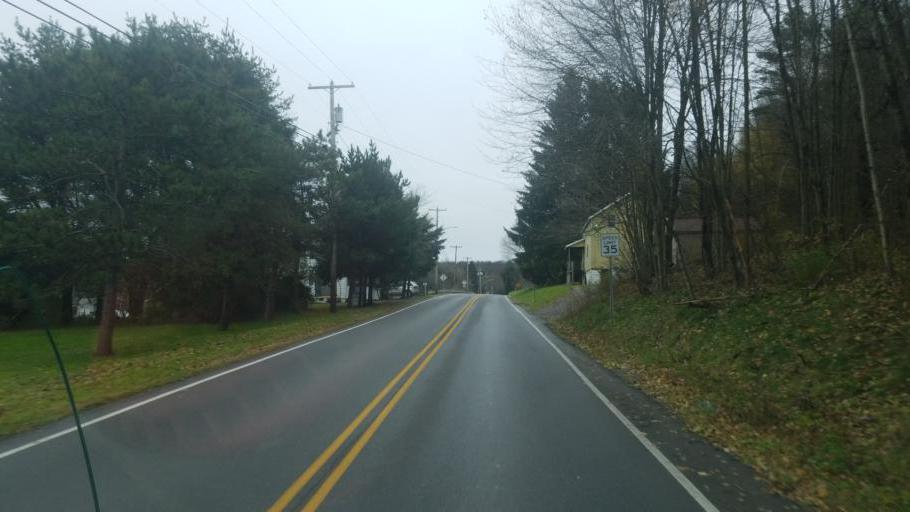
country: US
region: Pennsylvania
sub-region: Elk County
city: Saint Marys
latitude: 41.3552
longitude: -78.6095
